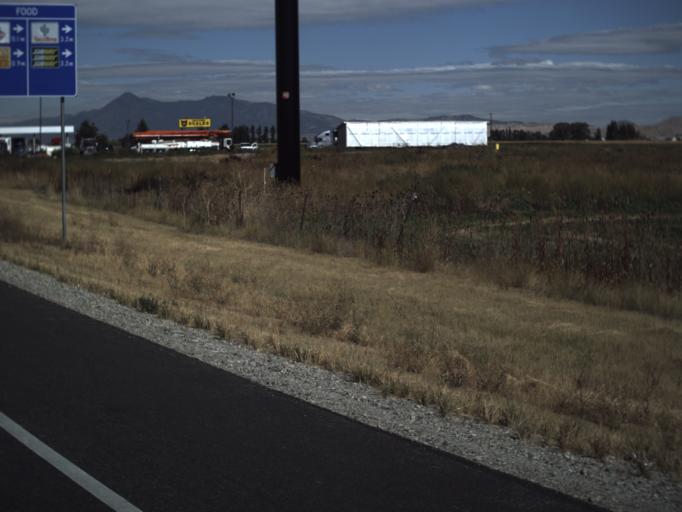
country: US
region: Utah
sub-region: Box Elder County
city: Elwood
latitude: 41.6802
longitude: -112.1396
